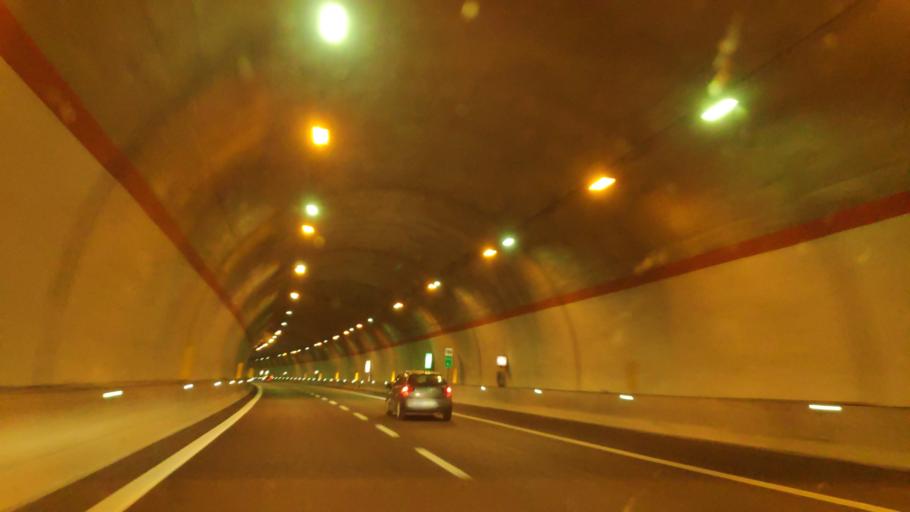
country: IT
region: Calabria
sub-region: Provincia di Cosenza
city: Morano Calabro
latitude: 39.8874
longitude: 16.1367
